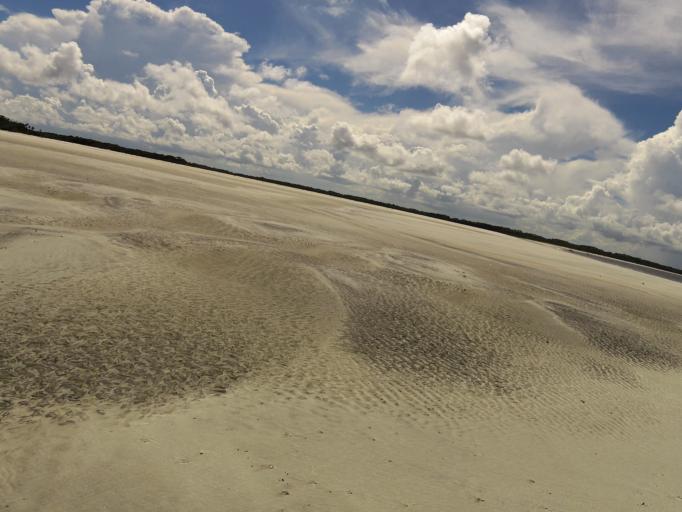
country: US
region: Florida
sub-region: Duval County
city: Atlantic Beach
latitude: 30.4880
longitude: -81.4180
